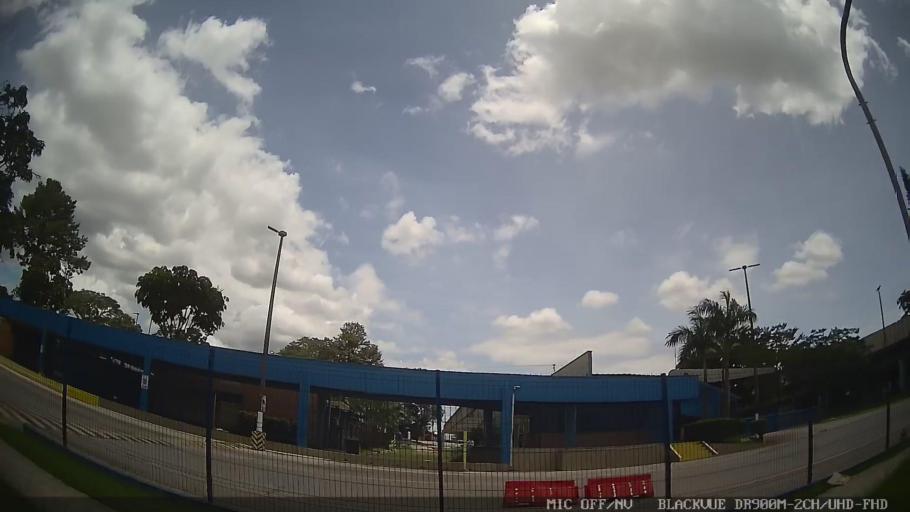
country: BR
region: Sao Paulo
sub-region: Suzano
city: Suzano
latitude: -23.5414
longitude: -46.2800
